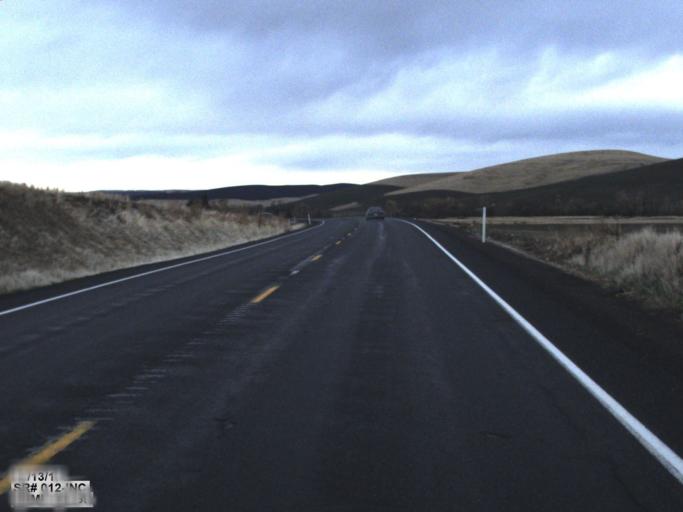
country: US
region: Washington
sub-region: Walla Walla County
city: Waitsburg
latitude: 46.2289
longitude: -118.1375
